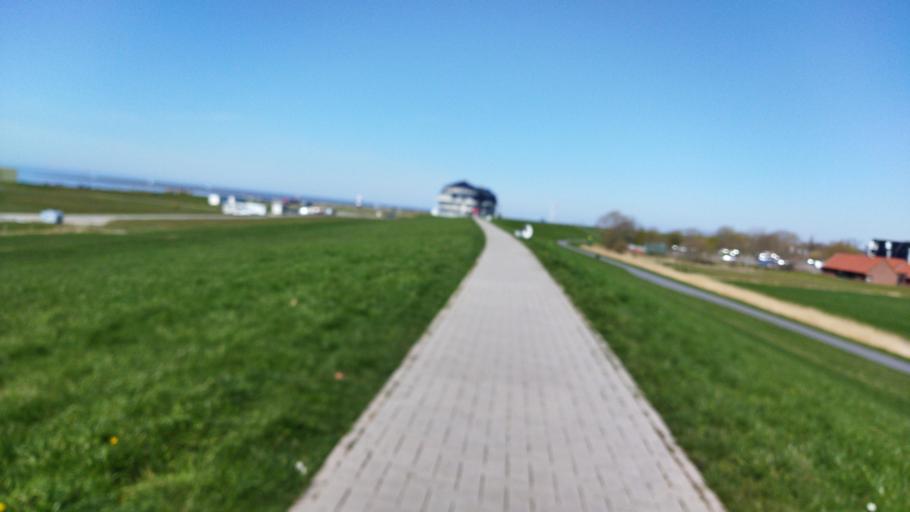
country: DE
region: Lower Saxony
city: Wremen
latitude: 53.6435
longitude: 8.4977
